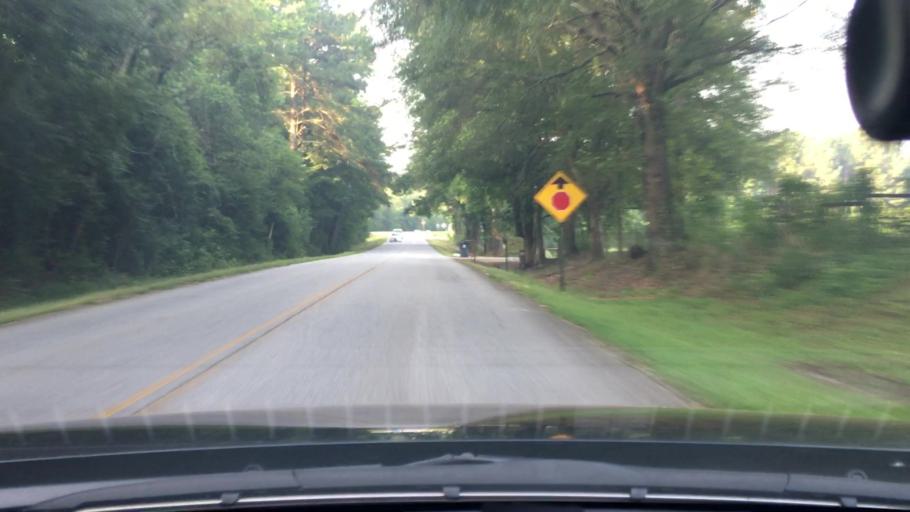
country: US
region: Georgia
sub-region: Fayette County
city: Peachtree City
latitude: 33.3936
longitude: -84.6241
